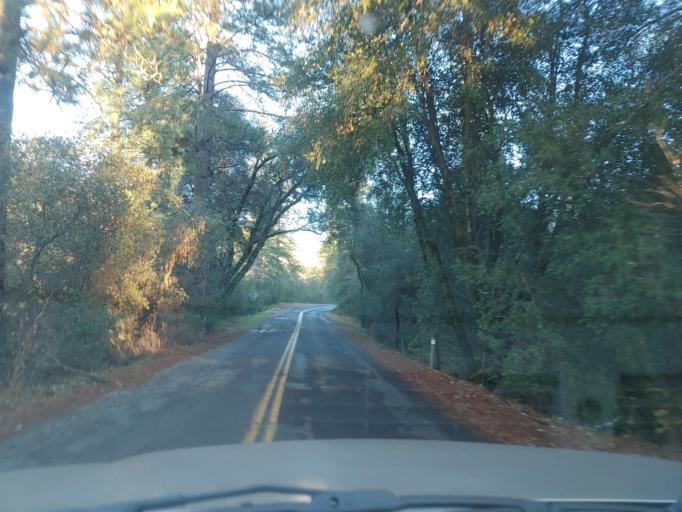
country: US
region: California
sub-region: Tuolumne County
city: Columbia
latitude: 38.0385
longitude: -120.3764
